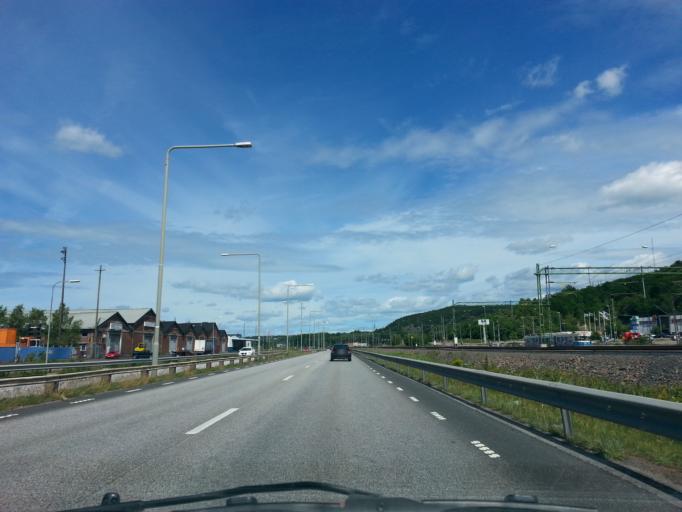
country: SE
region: Vaestra Goetaland
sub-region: Goteborg
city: Eriksbo
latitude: 57.7425
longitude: 12.0055
